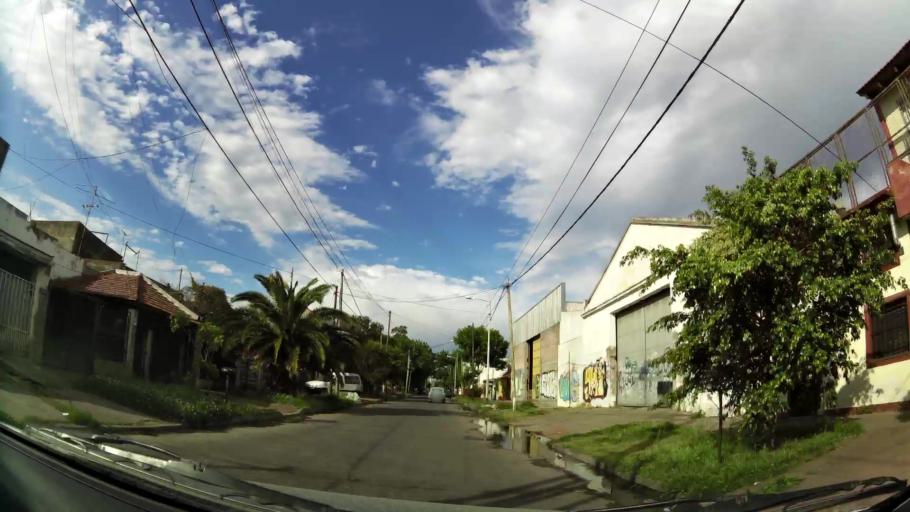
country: AR
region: Buenos Aires
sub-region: Partido de Lanus
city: Lanus
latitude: -34.6951
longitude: -58.3686
